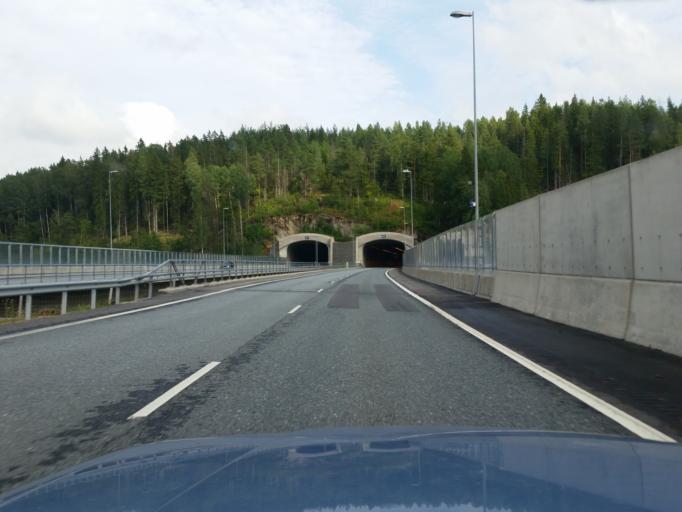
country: FI
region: Uusimaa
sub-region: Helsinki
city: Saukkola
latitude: 60.3125
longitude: 24.0022
